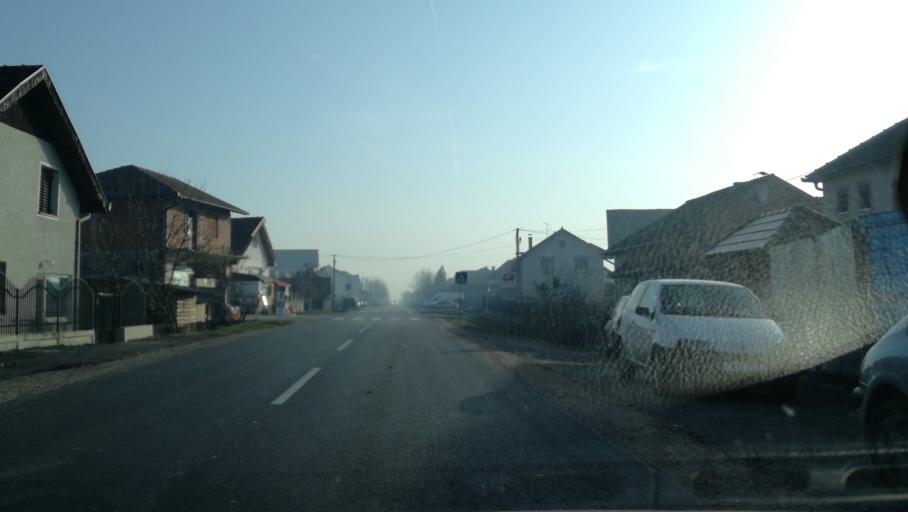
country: RS
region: Central Serbia
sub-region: Moravicki Okrug
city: Cacak
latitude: 43.9012
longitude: 20.3768
